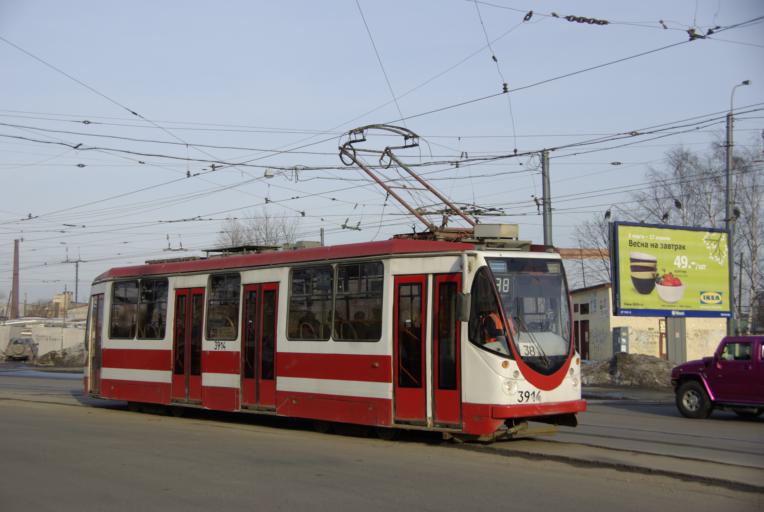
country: RU
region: Leningrad
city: Sampsonievskiy
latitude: 59.9912
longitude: 30.3524
